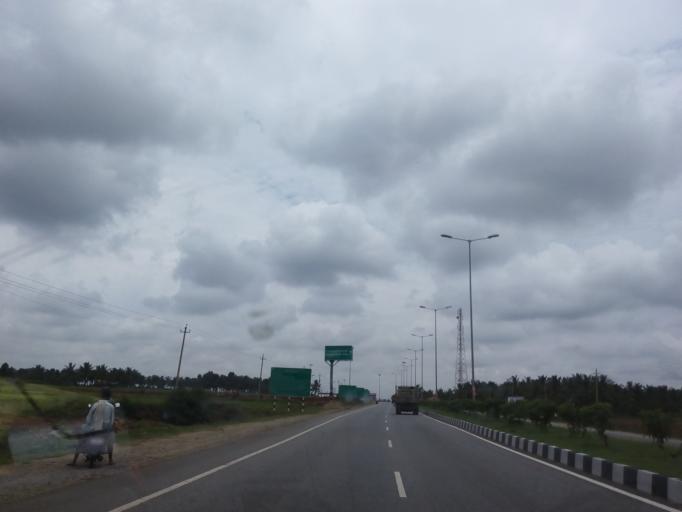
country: IN
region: Karnataka
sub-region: Hassan
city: Hassan
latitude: 12.9792
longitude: 76.2332
